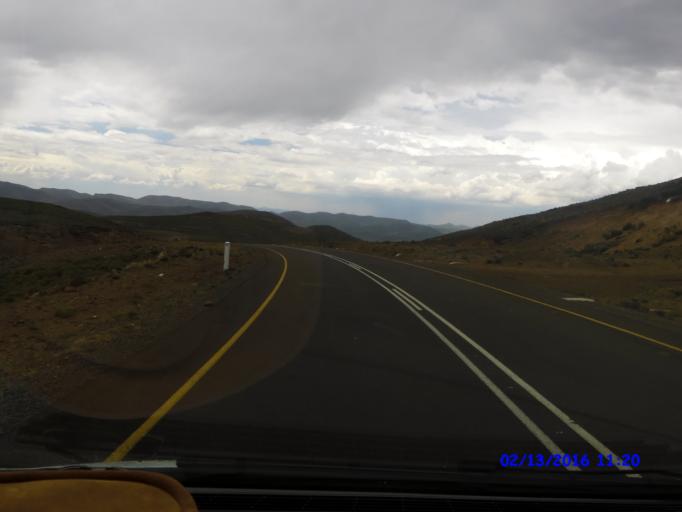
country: LS
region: Maseru
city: Nako
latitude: -29.7546
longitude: 27.9651
